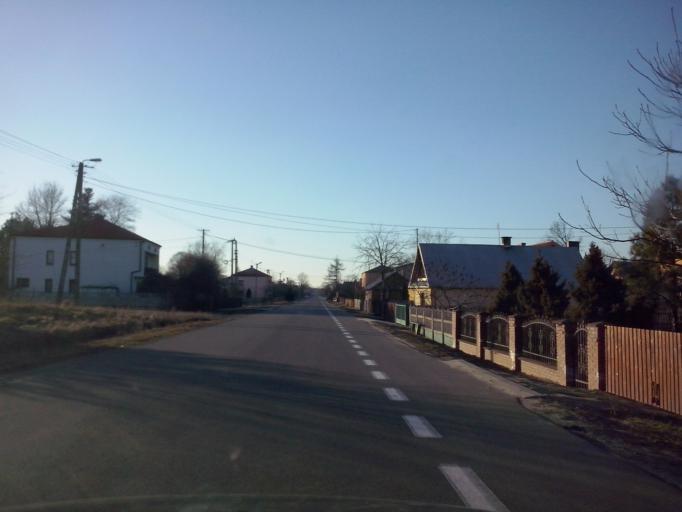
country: PL
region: Subcarpathian Voivodeship
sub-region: Powiat nizanski
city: Harasiuki
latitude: 50.4723
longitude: 22.4908
